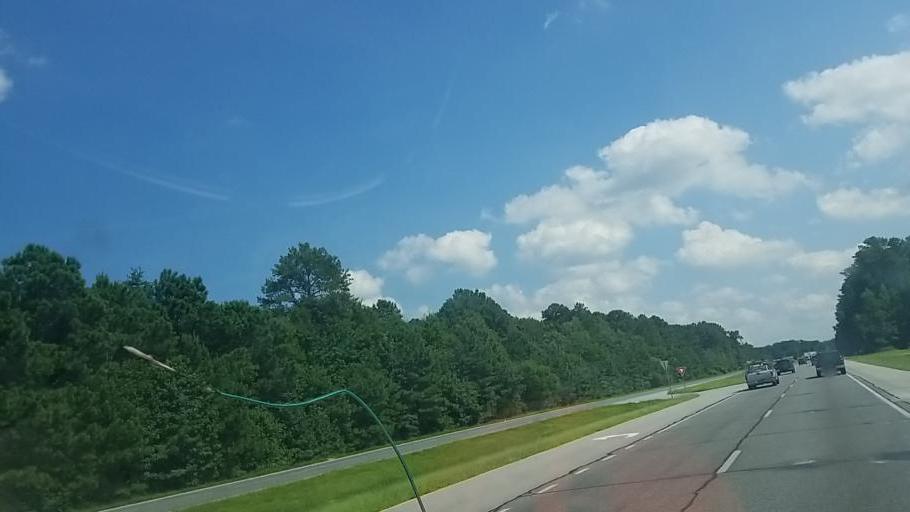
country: US
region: Delaware
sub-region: Sussex County
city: Georgetown
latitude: 38.7296
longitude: -75.4165
